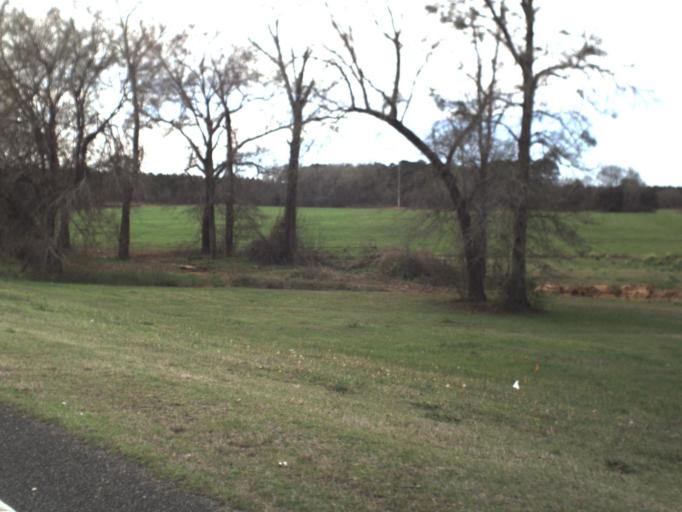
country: US
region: Florida
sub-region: Jackson County
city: Marianna
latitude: 30.8377
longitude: -85.3498
